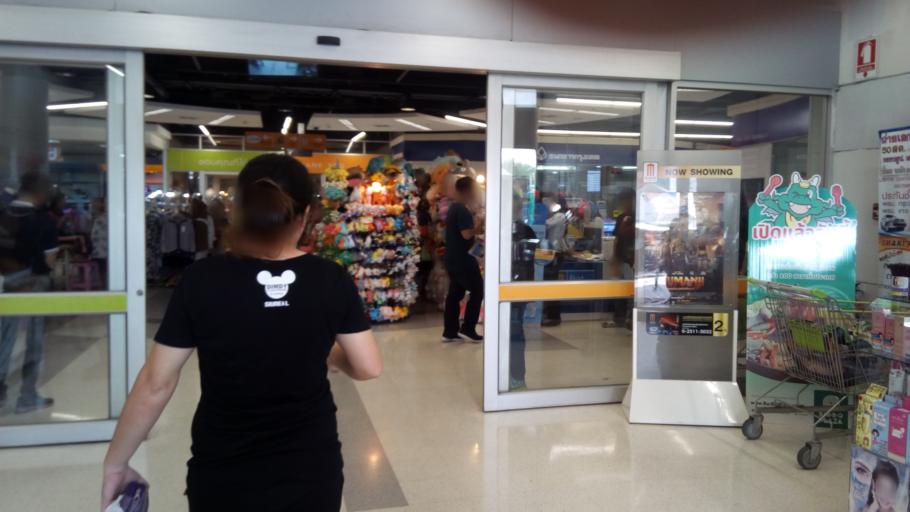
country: TH
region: Pathum Thani
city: Thanyaburi
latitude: 14.0250
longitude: 100.7433
